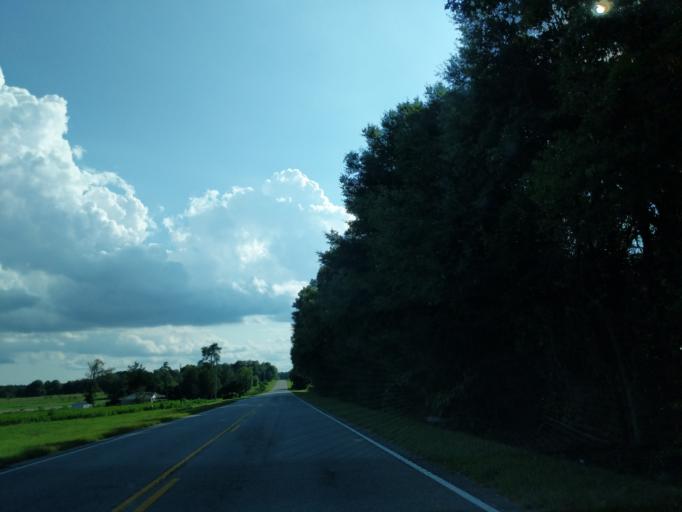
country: US
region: South Carolina
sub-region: Barnwell County
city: Williston
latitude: 33.4476
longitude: -81.3681
